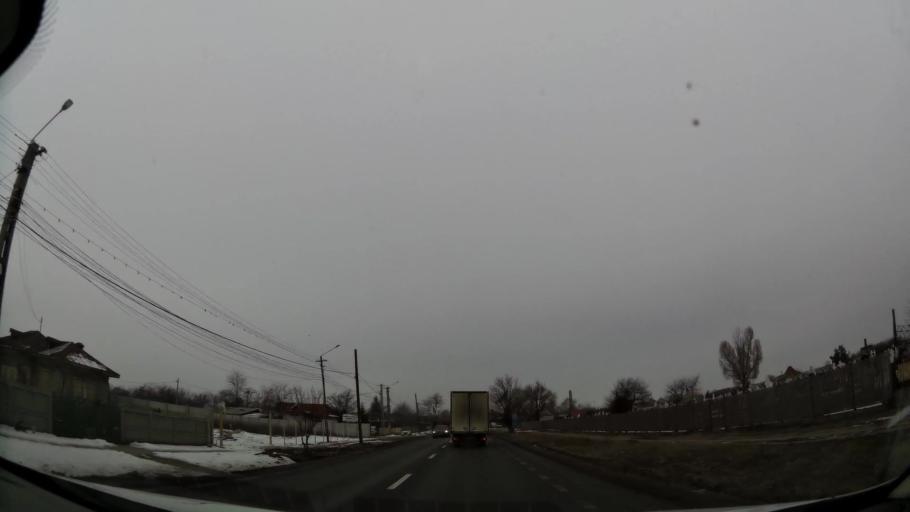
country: RO
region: Dambovita
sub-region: Comuna Racari
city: Racari
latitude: 44.6216
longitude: 25.7519
